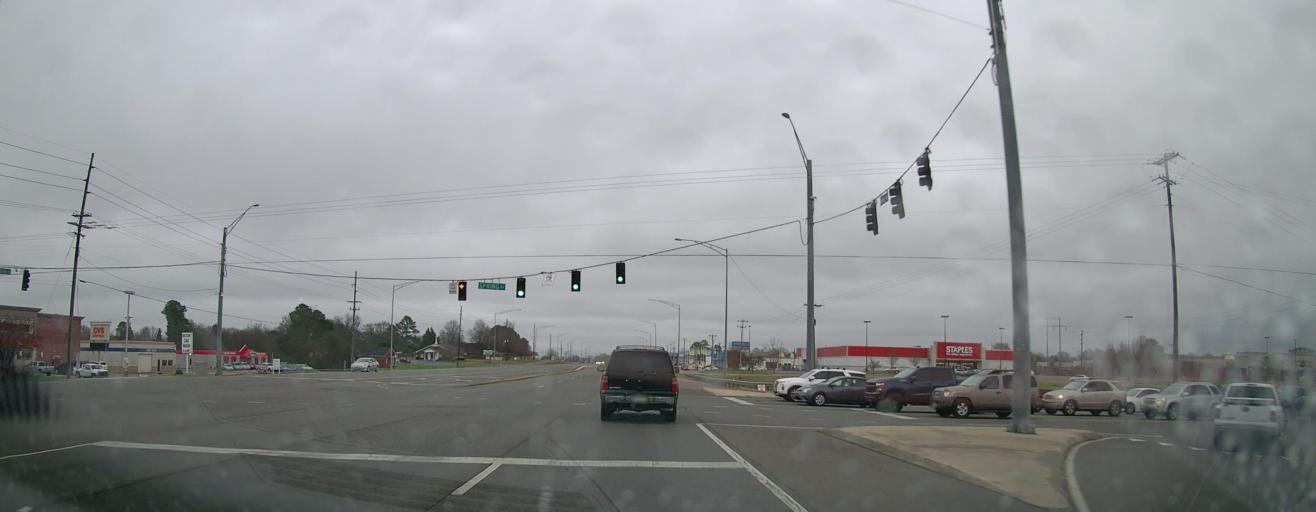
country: US
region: Alabama
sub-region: Morgan County
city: Flint City
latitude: 34.5599
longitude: -87.0004
